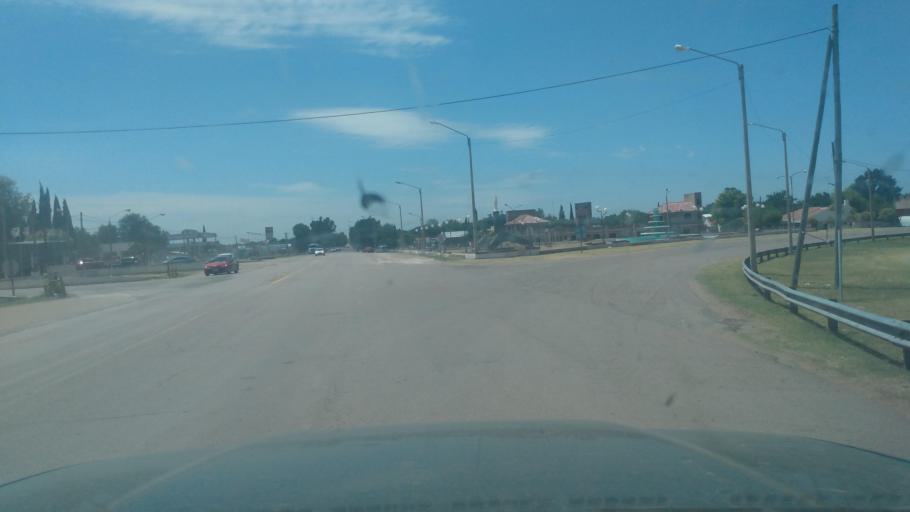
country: AR
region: La Pampa
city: General Acha
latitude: -37.3669
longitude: -64.6011
